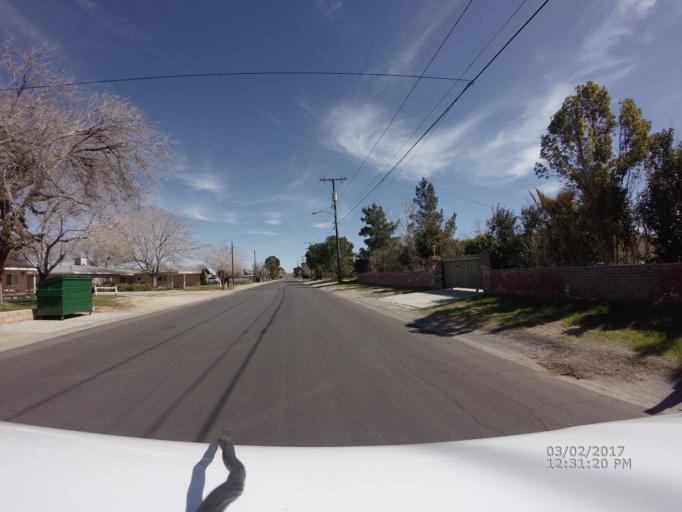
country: US
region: California
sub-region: Los Angeles County
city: Quartz Hill
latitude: 34.6511
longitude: -118.2162
